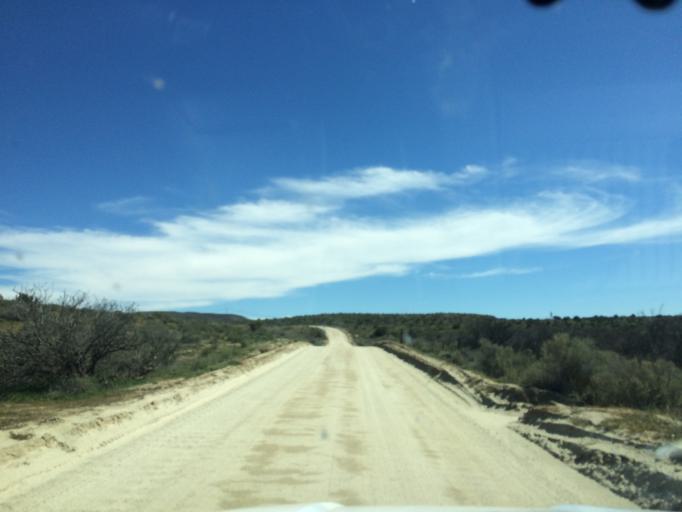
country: MX
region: Baja California
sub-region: Tecate
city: Cereso del Hongo
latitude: 32.6409
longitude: -116.1759
